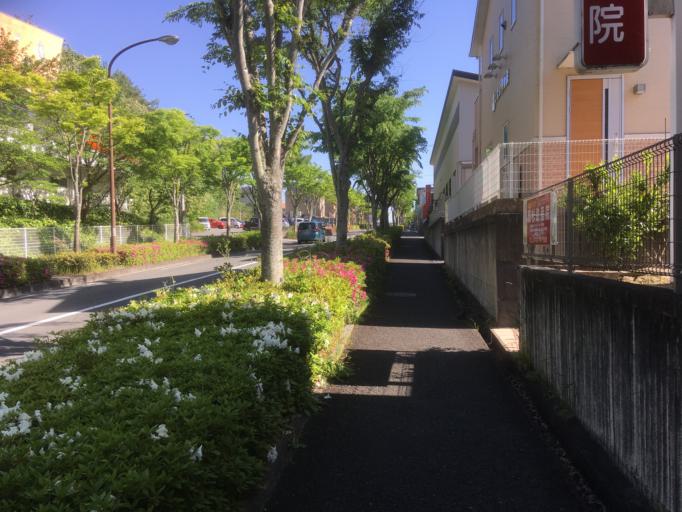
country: JP
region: Nara
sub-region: Ikoma-shi
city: Ikoma
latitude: 34.7243
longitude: 135.7158
